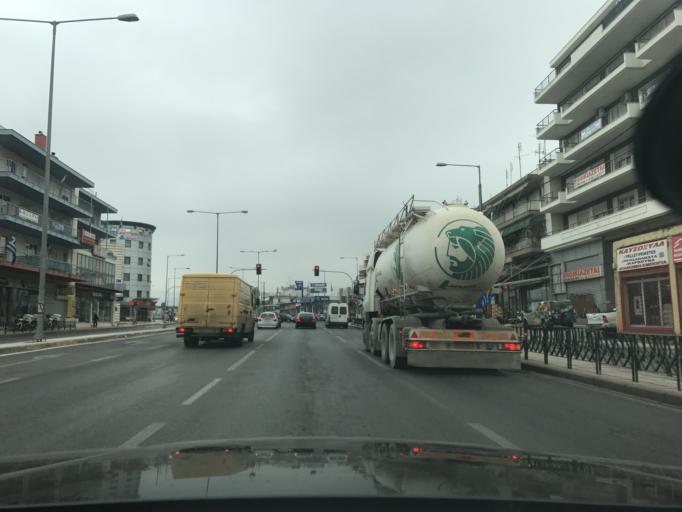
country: GR
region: Central Macedonia
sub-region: Nomos Thessalonikis
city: Stavroupoli
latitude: 40.6708
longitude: 22.9387
